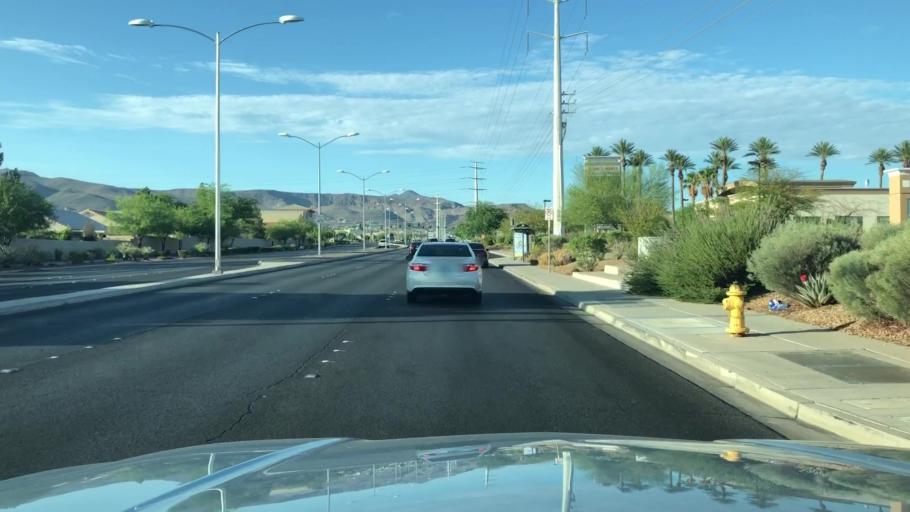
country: US
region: Nevada
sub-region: Clark County
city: Whitney
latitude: 36.0448
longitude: -115.0468
